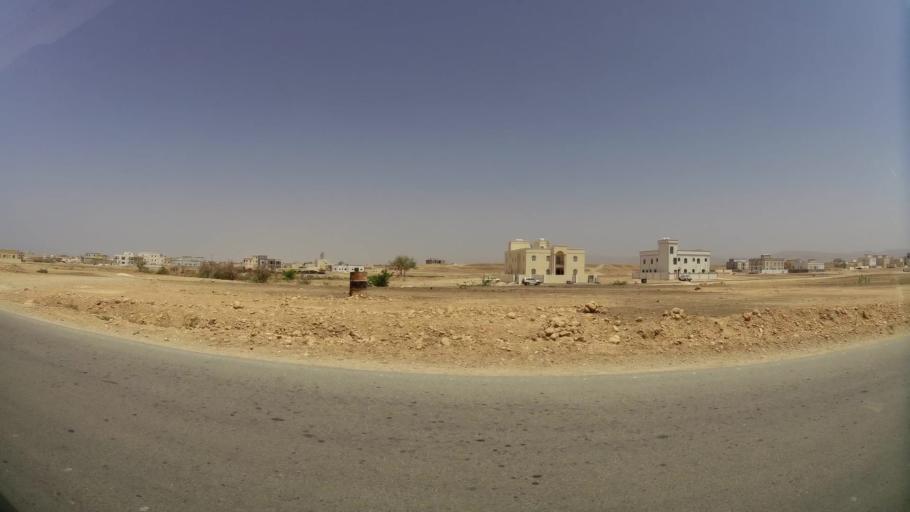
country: OM
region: Zufar
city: Salalah
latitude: 17.0768
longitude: 54.1915
